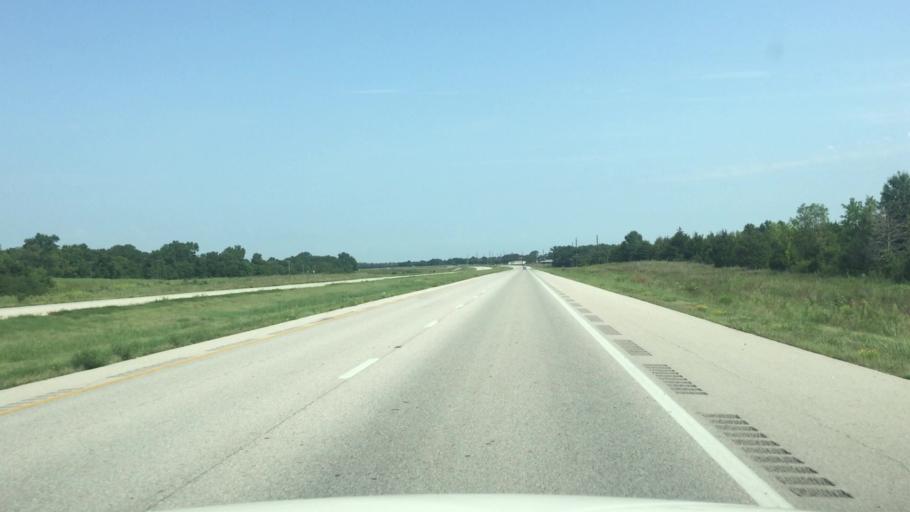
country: US
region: Kansas
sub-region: Montgomery County
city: Coffeyville
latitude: 37.0588
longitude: -95.5820
